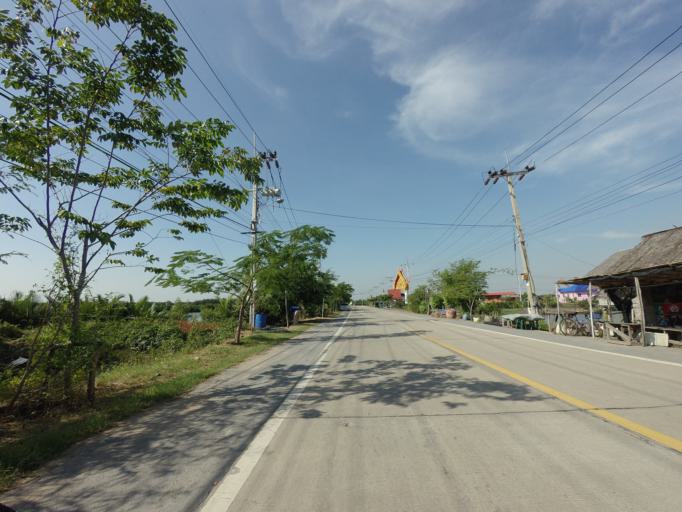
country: TH
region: Samut Prakan
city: Phra Samut Chedi
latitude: 13.5594
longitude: 100.5411
